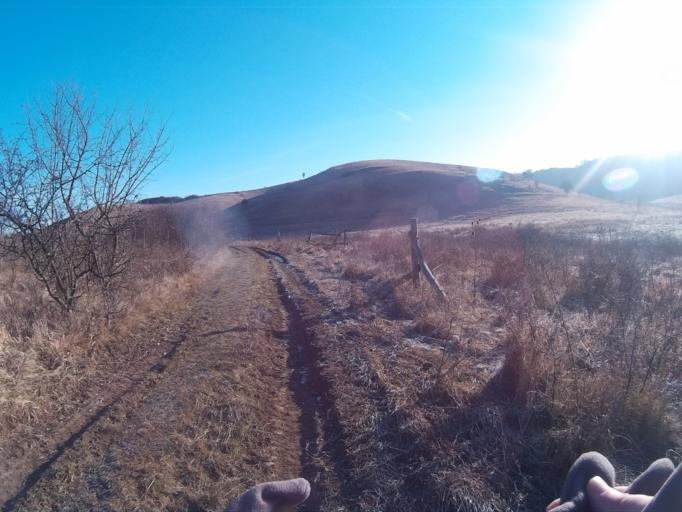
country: HU
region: Borsod-Abauj-Zemplen
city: Putnok
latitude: 48.3828
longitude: 20.4637
